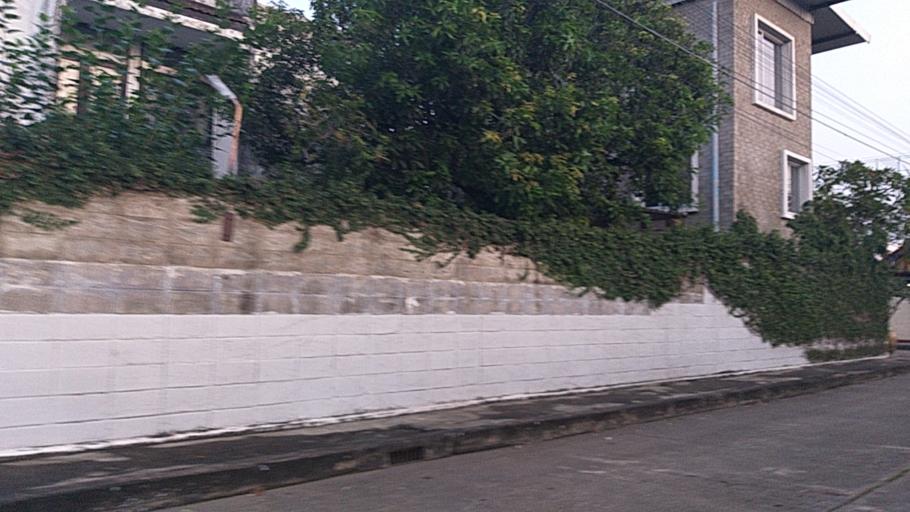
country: TH
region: Bangkok
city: Lat Phrao
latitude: 13.8270
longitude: 100.6099
